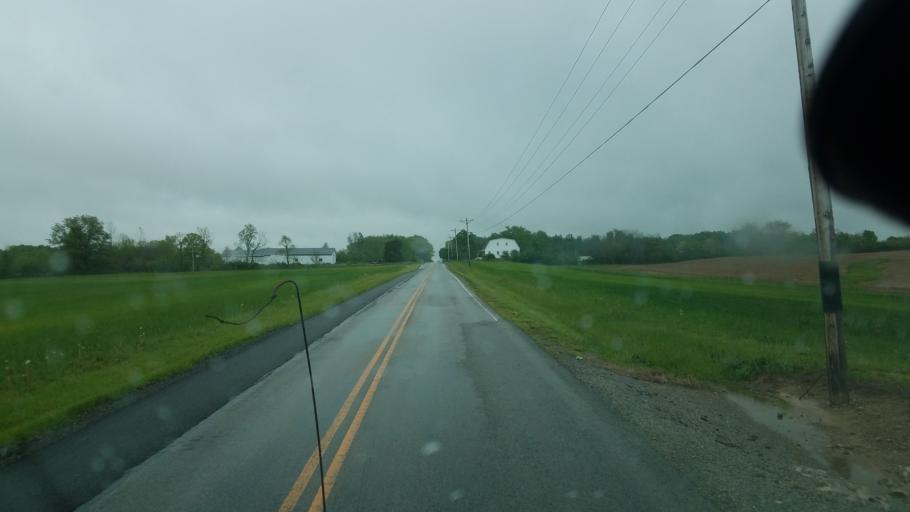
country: US
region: Ohio
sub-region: Highland County
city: Greenfield
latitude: 39.3417
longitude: -83.4449
